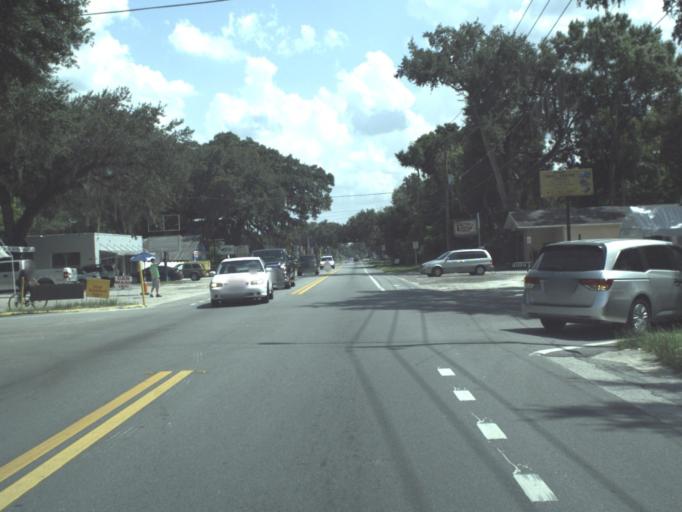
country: US
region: Florida
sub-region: Pasco County
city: Zephyrhills
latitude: 28.2267
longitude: -82.1800
